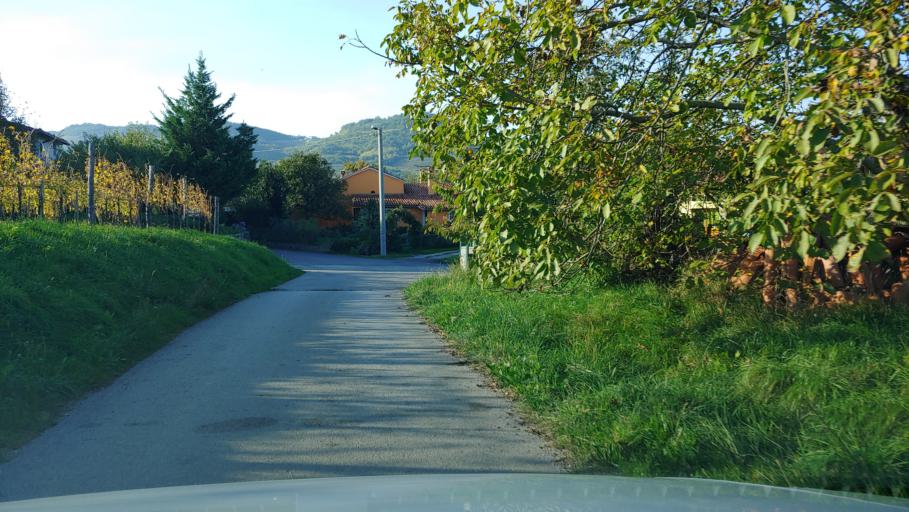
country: SI
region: Vipava
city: Vipava
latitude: 45.8355
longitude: 13.9360
